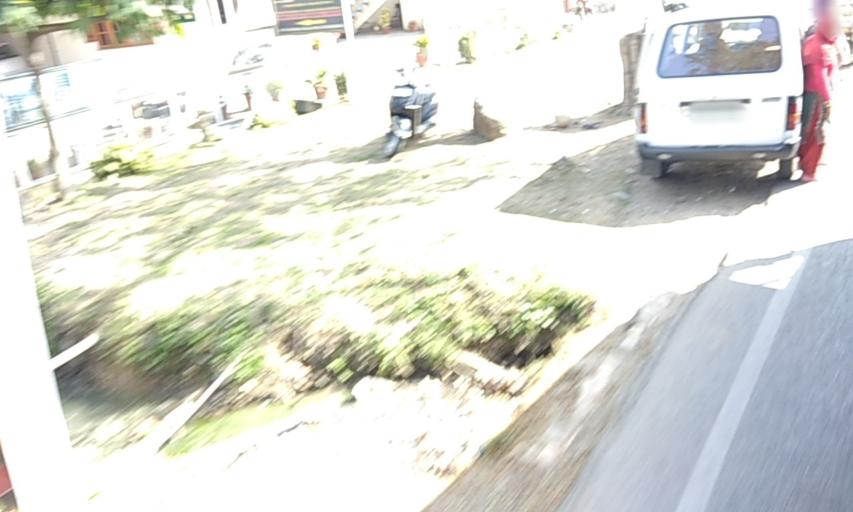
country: IN
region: Himachal Pradesh
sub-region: Kangra
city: Yol
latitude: 32.2155
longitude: 76.1805
